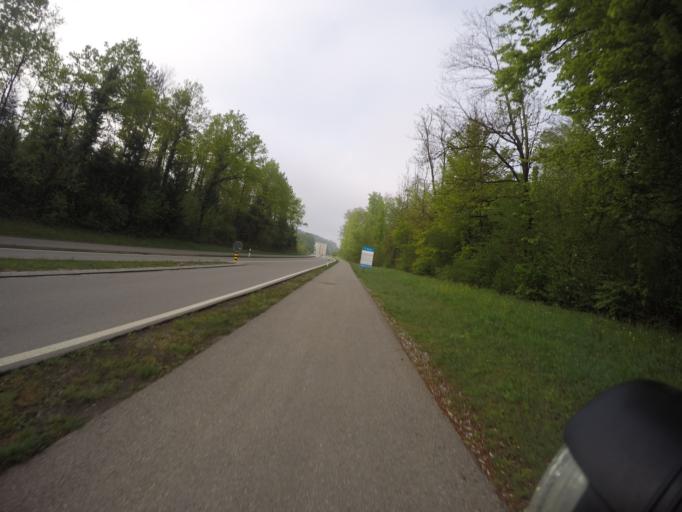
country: CH
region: Zurich
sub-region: Bezirk Pfaeffikon
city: Tagelswangen
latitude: 47.4369
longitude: 8.6812
